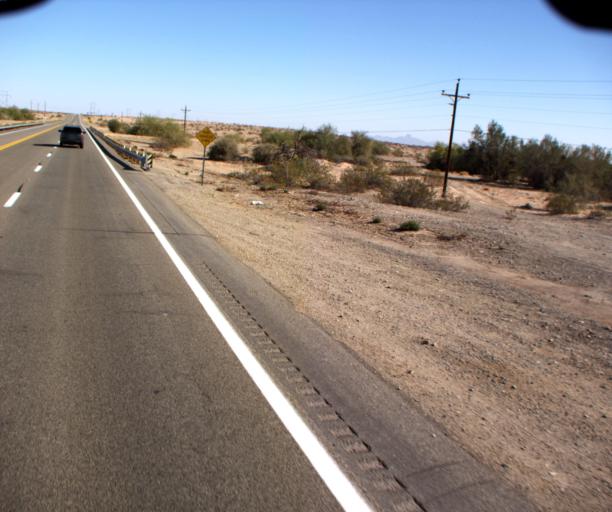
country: US
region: Arizona
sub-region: Yuma County
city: Fortuna Foothills
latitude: 32.7980
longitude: -114.3810
